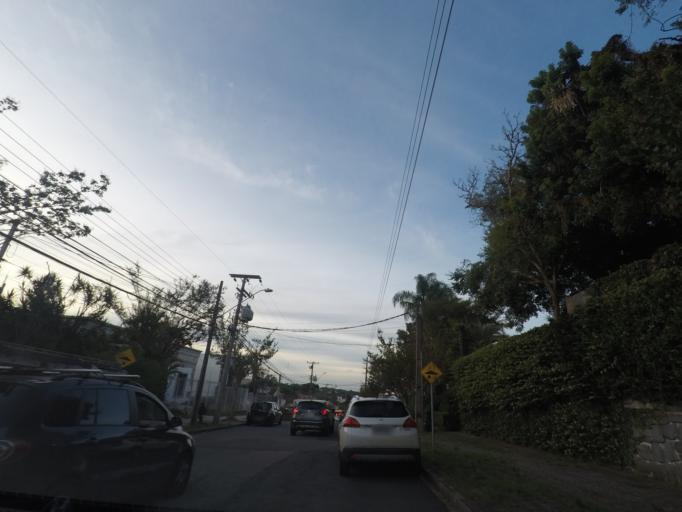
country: BR
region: Parana
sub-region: Curitiba
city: Curitiba
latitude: -25.4208
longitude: -49.2846
